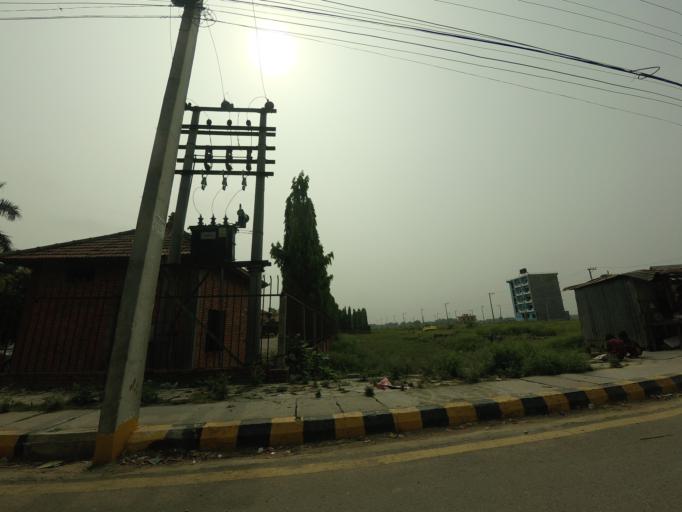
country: IN
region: Uttar Pradesh
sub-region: Maharajganj
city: Nautanwa
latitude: 27.4685
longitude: 83.2839
